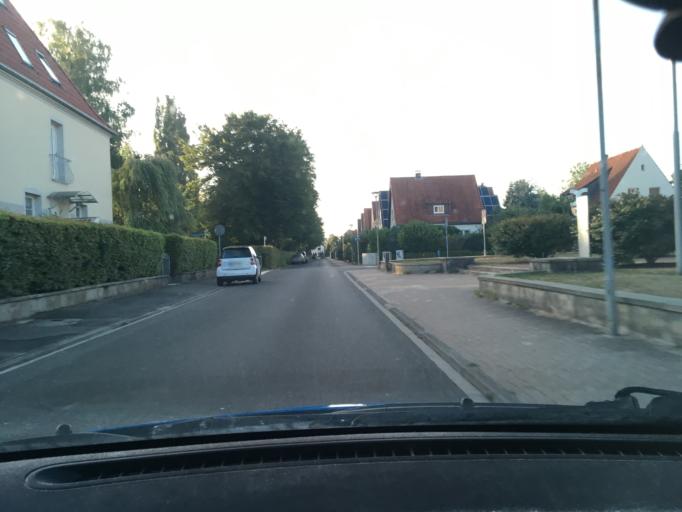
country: DE
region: Lower Saxony
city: Celle
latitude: 52.6312
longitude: 10.0984
